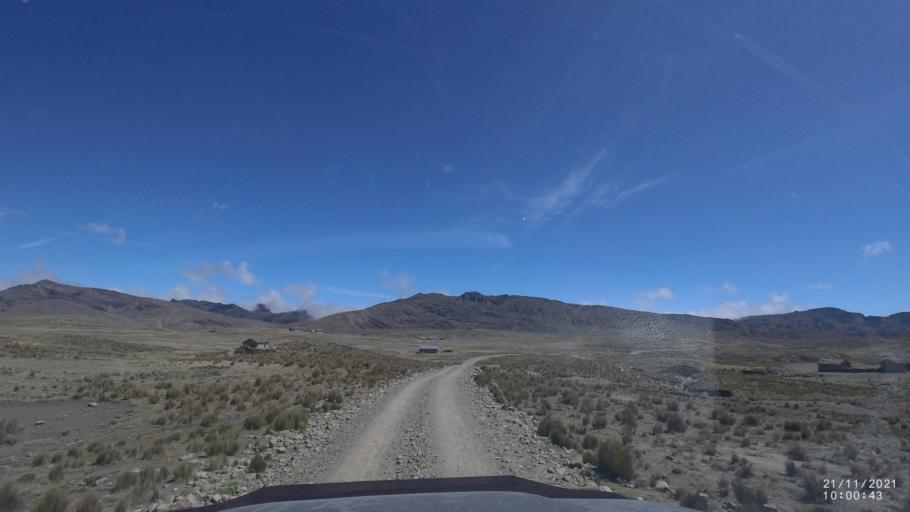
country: BO
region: Cochabamba
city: Cochabamba
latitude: -17.0343
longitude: -66.2794
